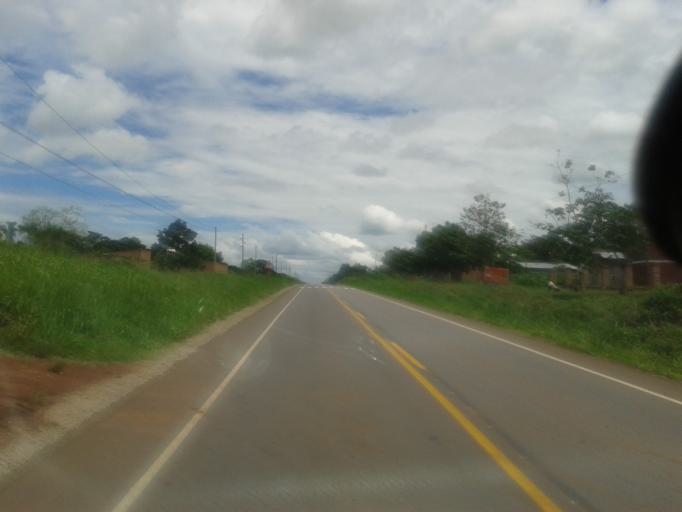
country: UG
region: Western Region
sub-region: Kiryandongo District
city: Kiryandongo
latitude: 1.8677
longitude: 32.0519
